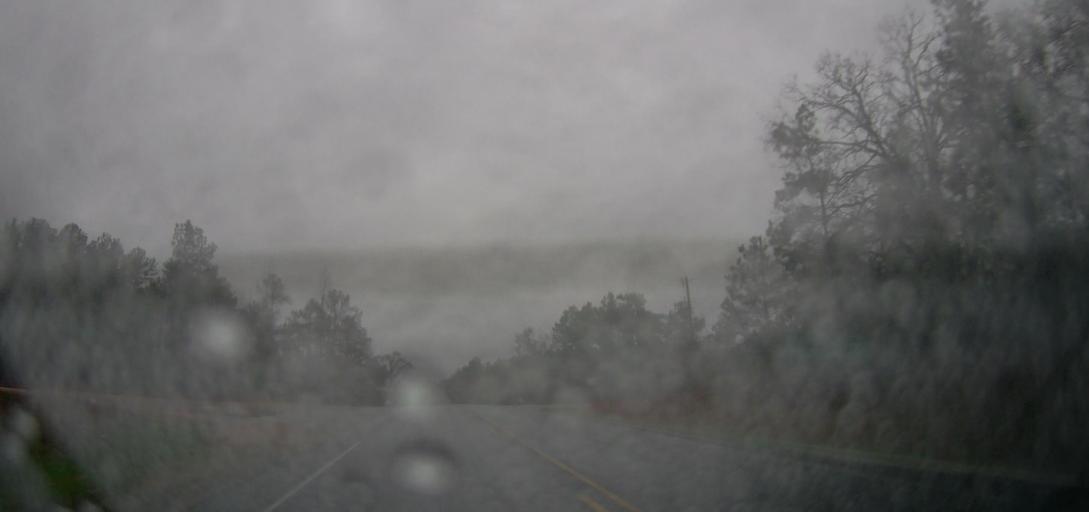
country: US
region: Alabama
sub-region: Autauga County
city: Pine Level
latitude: 32.5974
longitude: -86.7084
